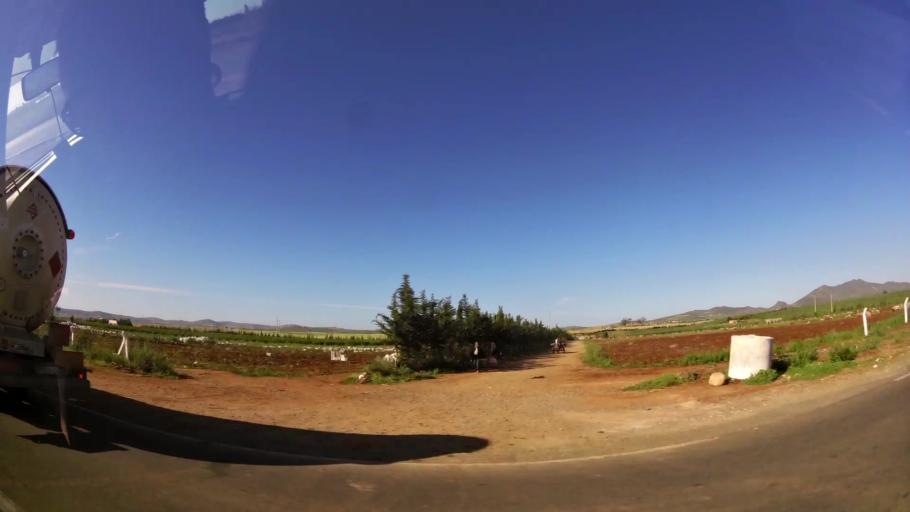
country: MA
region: Oriental
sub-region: Berkane-Taourirt
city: Ahfir
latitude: 34.9979
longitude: -2.1705
